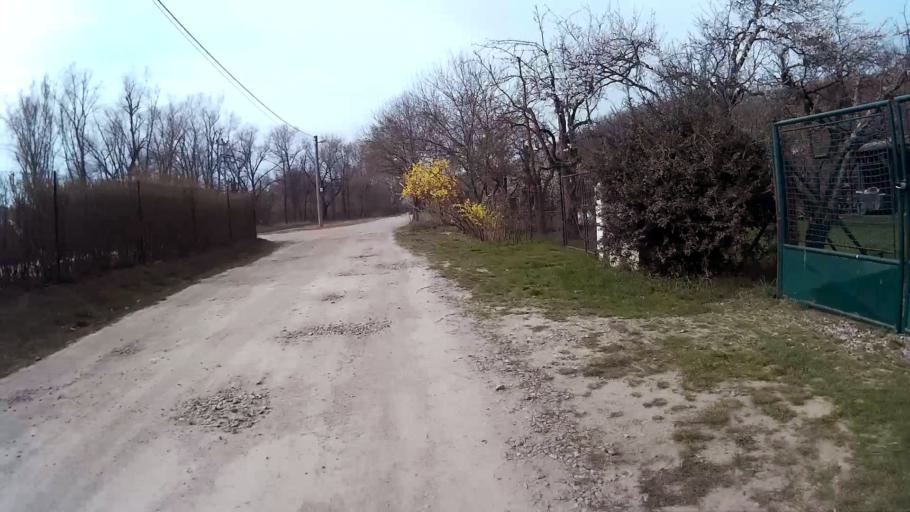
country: CZ
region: South Moravian
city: Dolni Kounice
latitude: 49.0621
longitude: 16.4805
